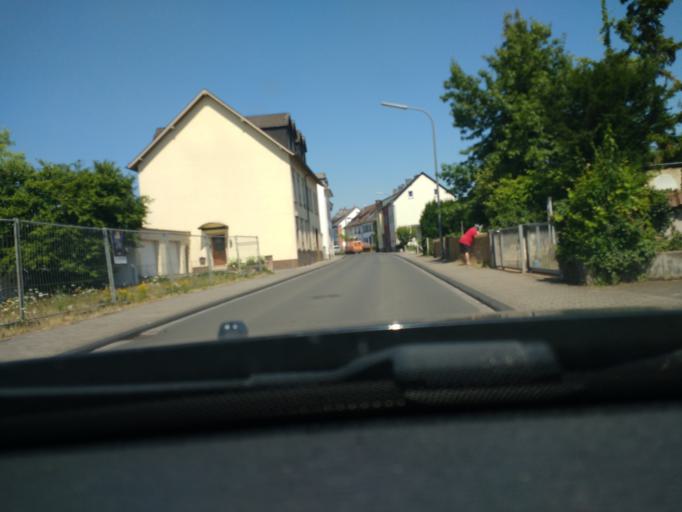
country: DE
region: Rheinland-Pfalz
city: Wittlich
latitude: 49.9882
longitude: 6.8914
